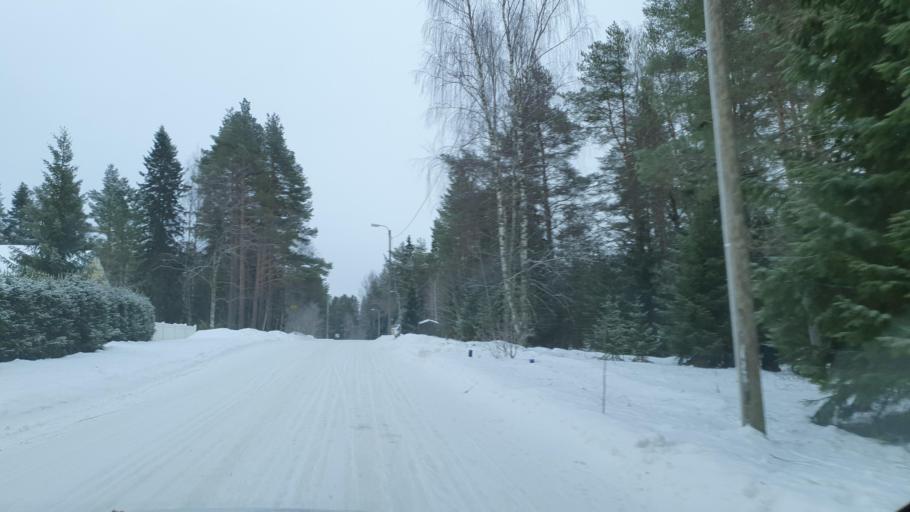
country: FI
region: Northern Ostrobothnia
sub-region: Oulu
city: Haukipudas
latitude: 65.1932
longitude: 25.4151
